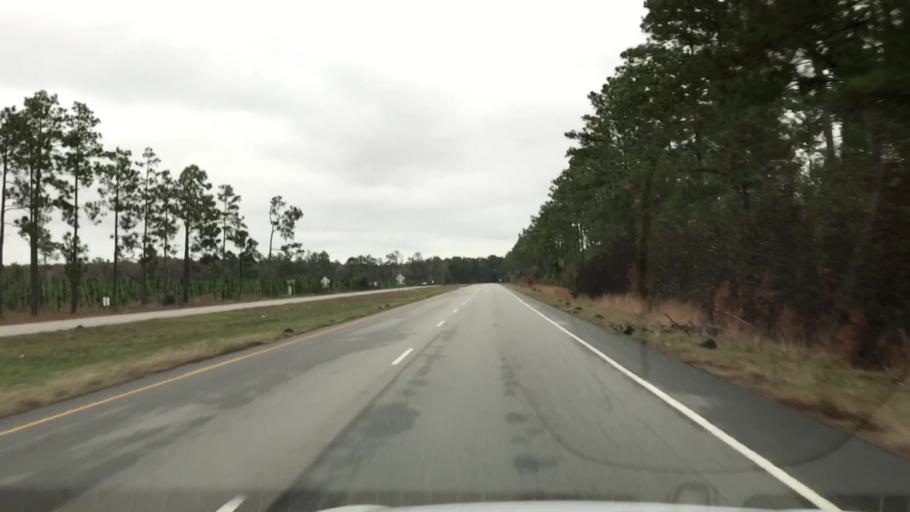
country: US
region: South Carolina
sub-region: Georgetown County
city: Georgetown
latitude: 33.1748
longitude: -79.4164
